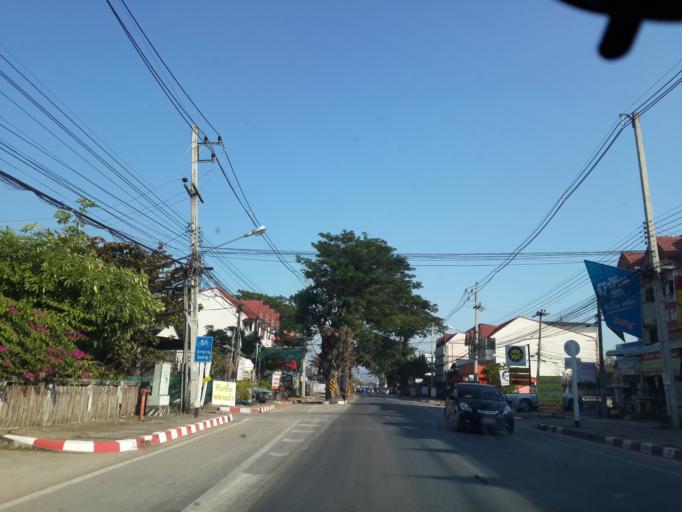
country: TH
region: Chiang Mai
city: San Kamphaeng
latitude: 18.7490
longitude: 99.1121
